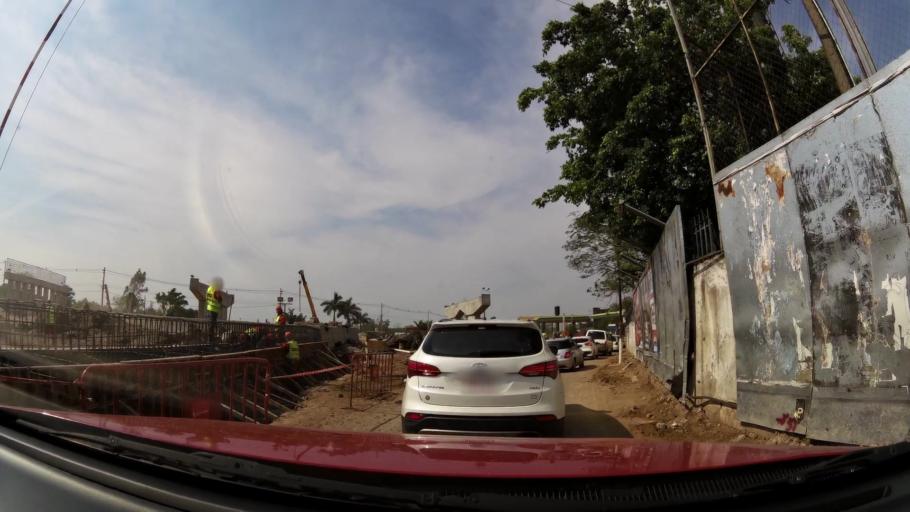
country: PY
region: Central
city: Fernando de la Mora
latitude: -25.2747
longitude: -57.5453
